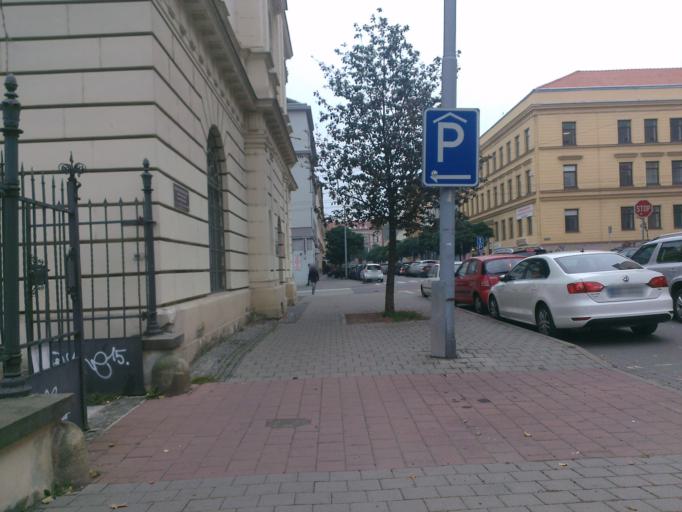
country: CZ
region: South Moravian
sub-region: Mesto Brno
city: Brno
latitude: 49.2017
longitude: 16.6024
